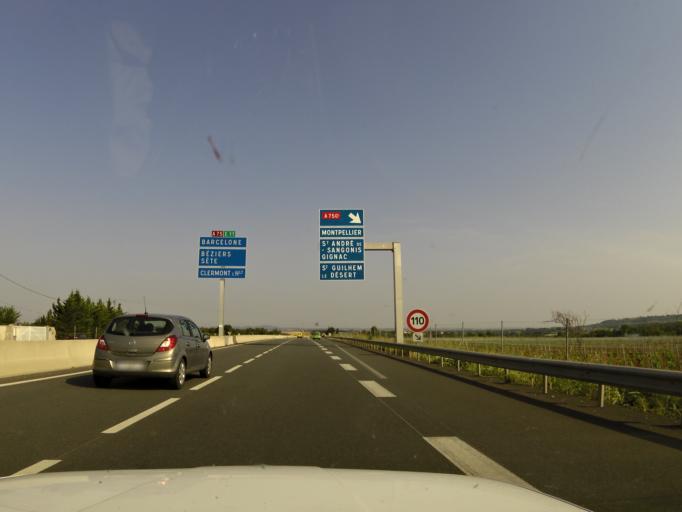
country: FR
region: Languedoc-Roussillon
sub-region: Departement de l'Herault
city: Nebian
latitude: 43.6595
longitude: 3.4428
